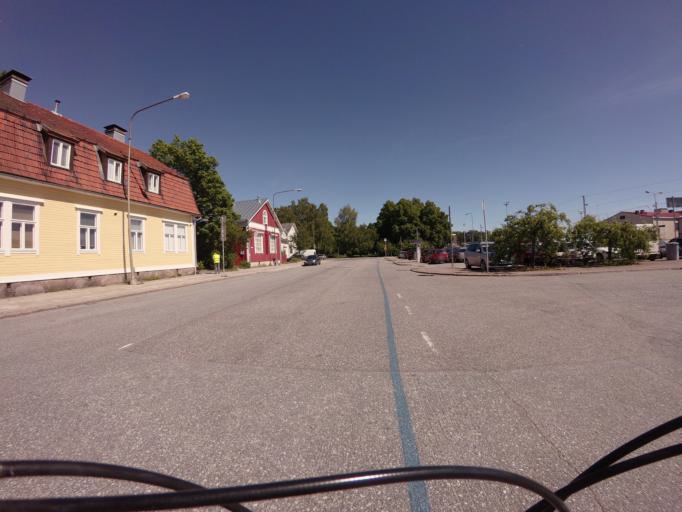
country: FI
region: Varsinais-Suomi
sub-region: Turku
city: Turku
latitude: 60.4348
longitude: 22.2249
